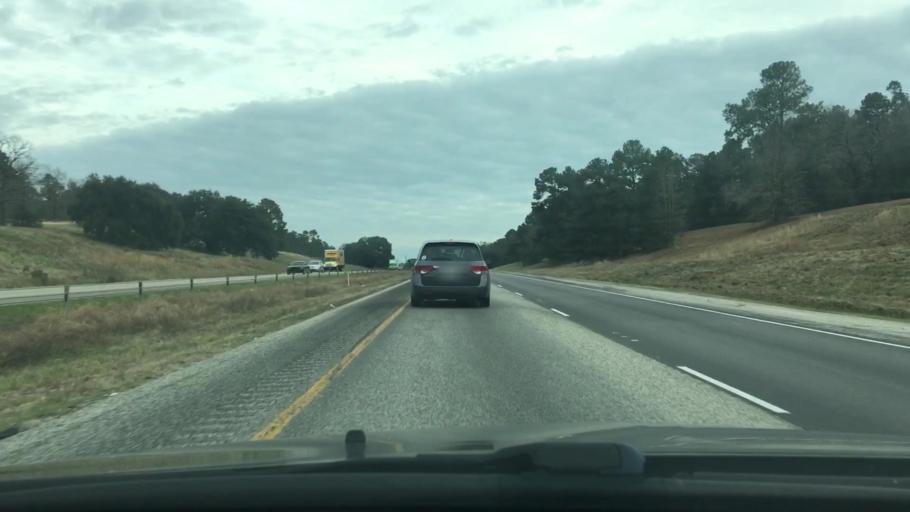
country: US
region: Texas
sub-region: Walker County
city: Huntsville
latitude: 30.8167
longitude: -95.6991
